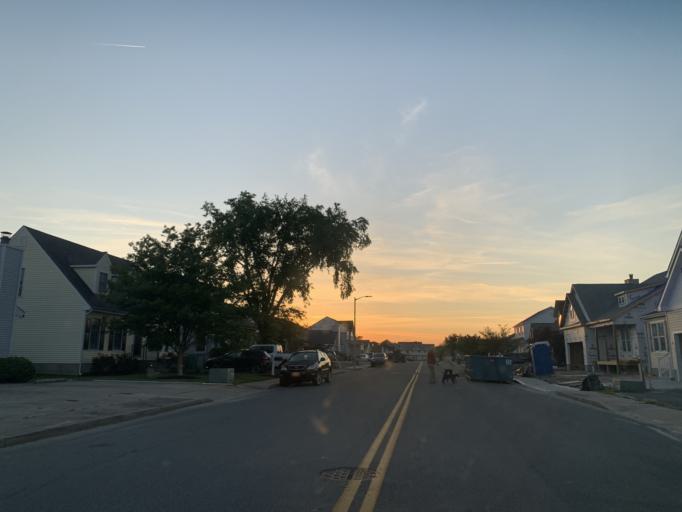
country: US
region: Delaware
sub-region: Sussex County
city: Bethany Beach
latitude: 38.4485
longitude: -75.0627
